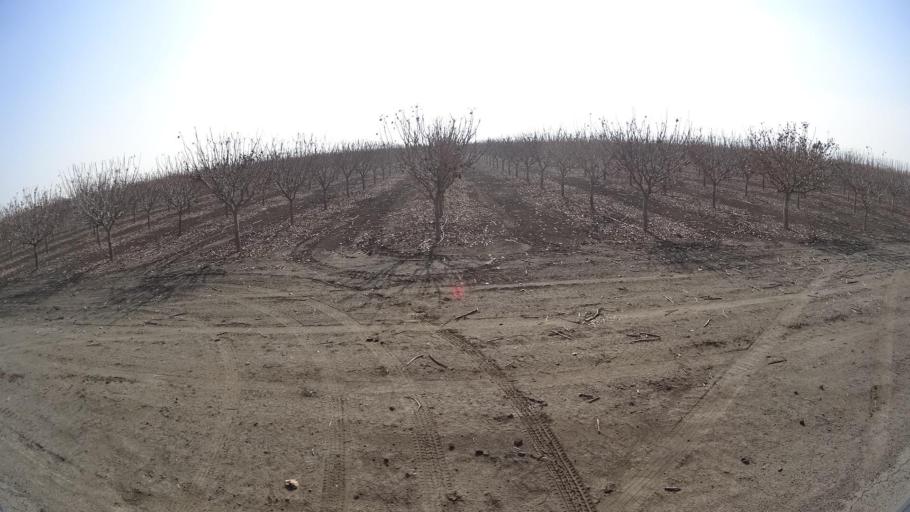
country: US
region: California
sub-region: Kern County
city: Buttonwillow
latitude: 35.3402
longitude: -119.4094
